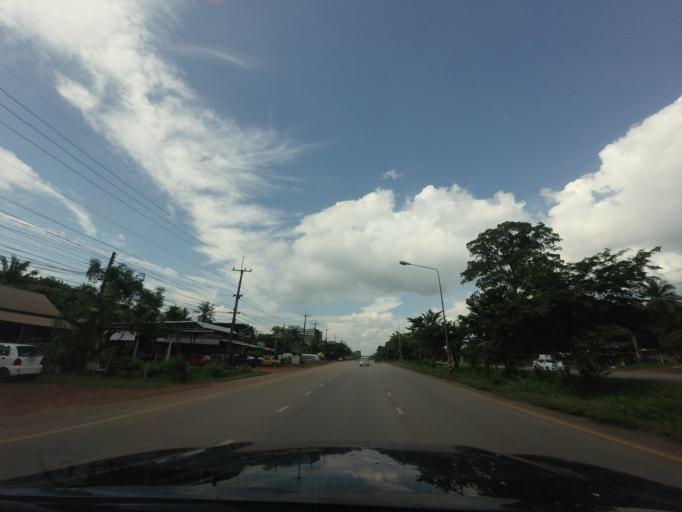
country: TH
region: Changwat Udon Thani
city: Udon Thani
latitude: 17.5463
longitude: 102.8005
